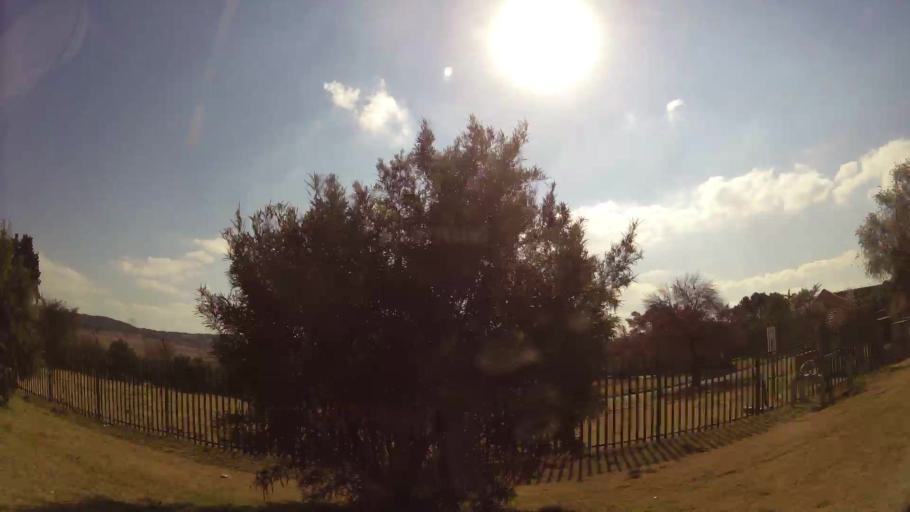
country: ZA
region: Gauteng
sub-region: City of Johannesburg Metropolitan Municipality
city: Midrand
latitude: -26.0083
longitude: 28.0720
